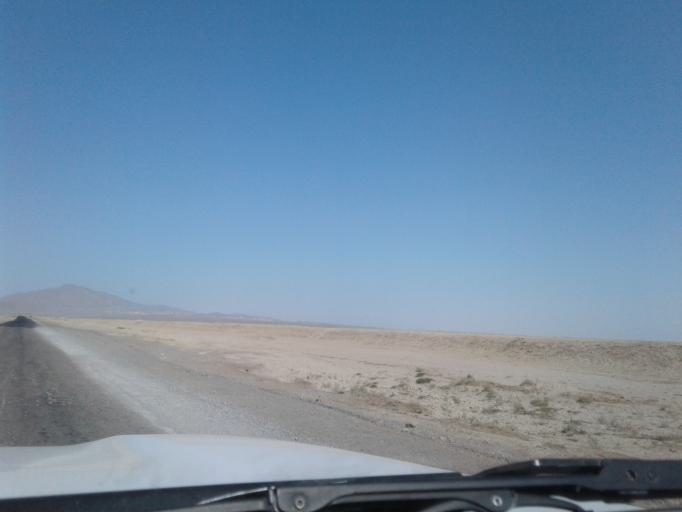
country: TM
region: Balkan
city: Gumdag
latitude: 39.2261
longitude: 54.6719
